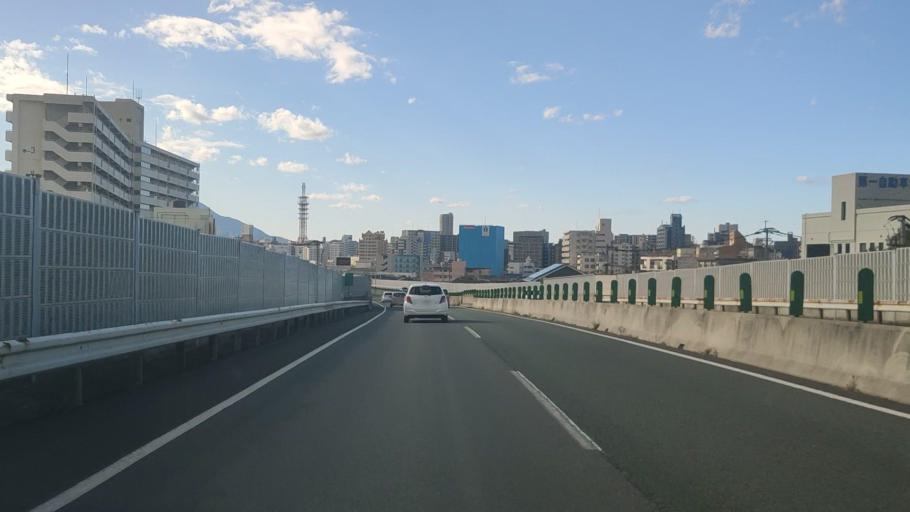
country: JP
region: Fukuoka
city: Kitakyushu
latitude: 33.8789
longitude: 130.8972
